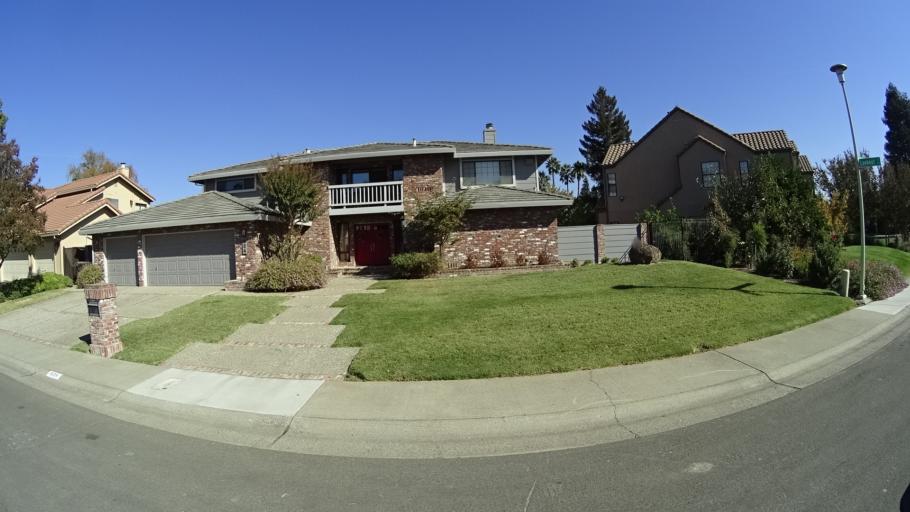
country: US
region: California
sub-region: Yolo County
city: West Sacramento
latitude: 38.5100
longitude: -121.5388
